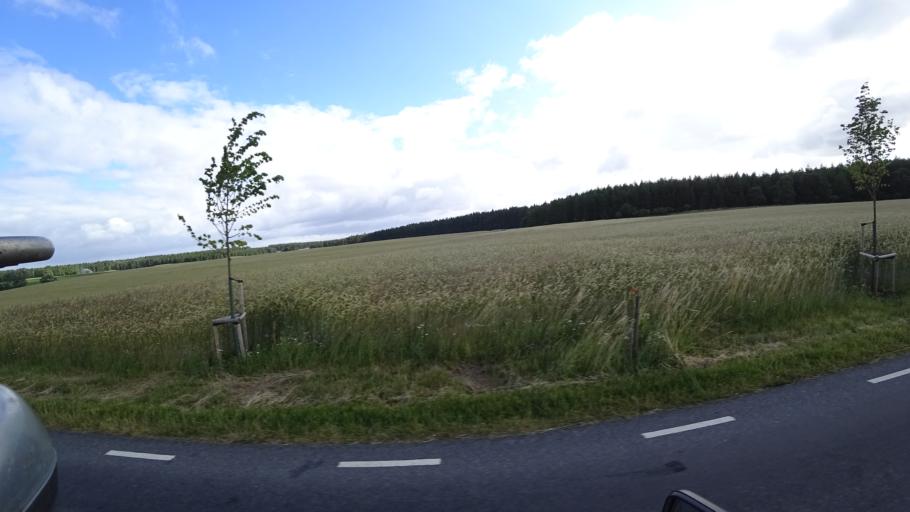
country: SE
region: Skane
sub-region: Kristianstads Kommun
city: Degeberga
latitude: 55.8631
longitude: 14.0601
